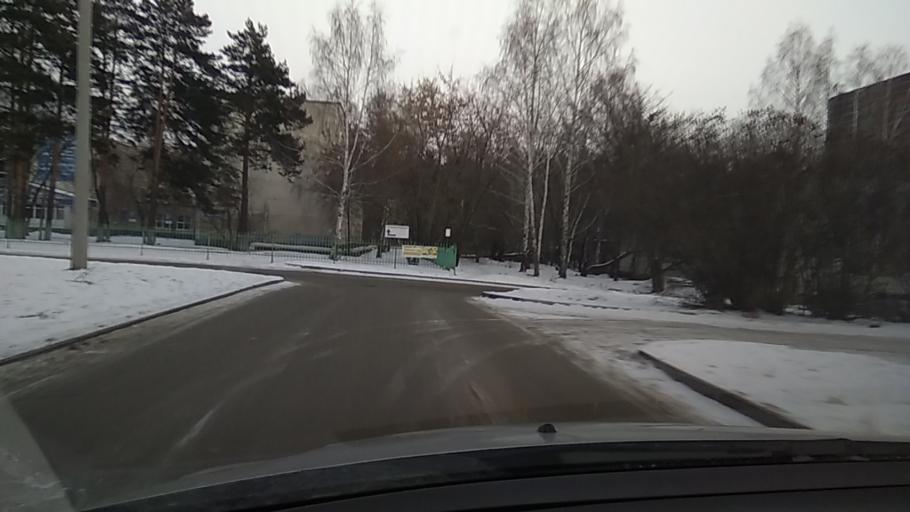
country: RU
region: Sverdlovsk
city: Istok
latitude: 56.7624
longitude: 60.7161
